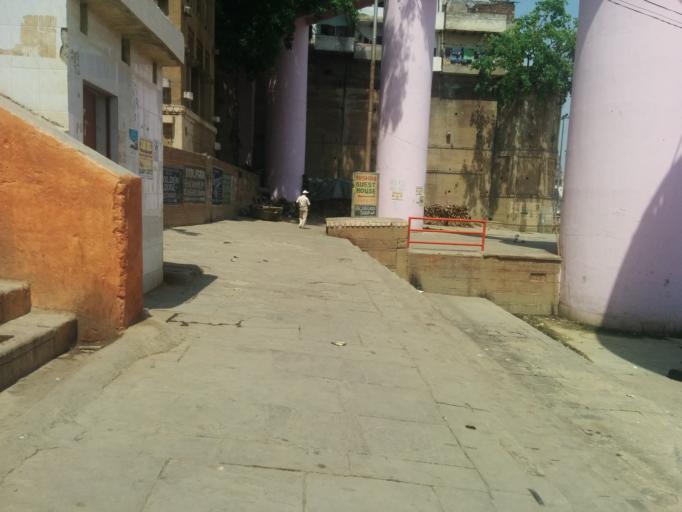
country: IN
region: Uttar Pradesh
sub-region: Varanasi
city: Varanasi
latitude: 25.3101
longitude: 83.0133
